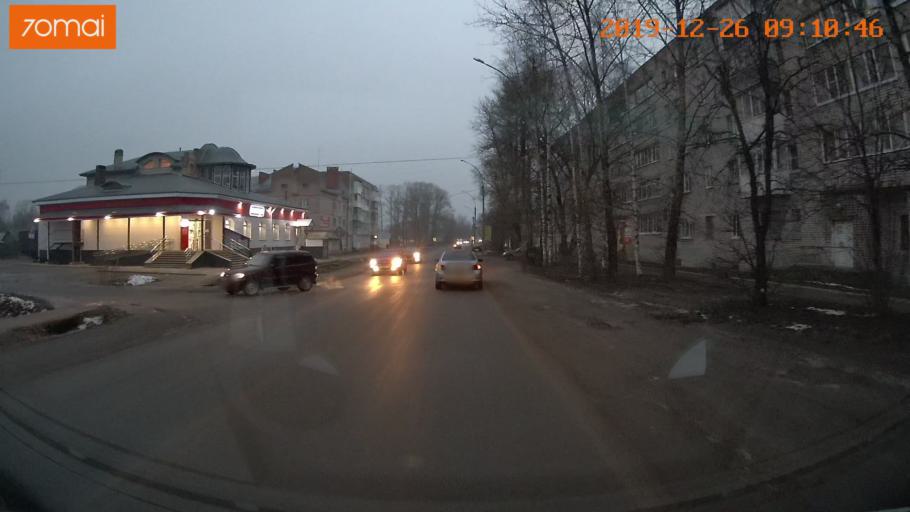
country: RU
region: Vologda
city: Gryazovets
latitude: 58.8727
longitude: 40.2525
